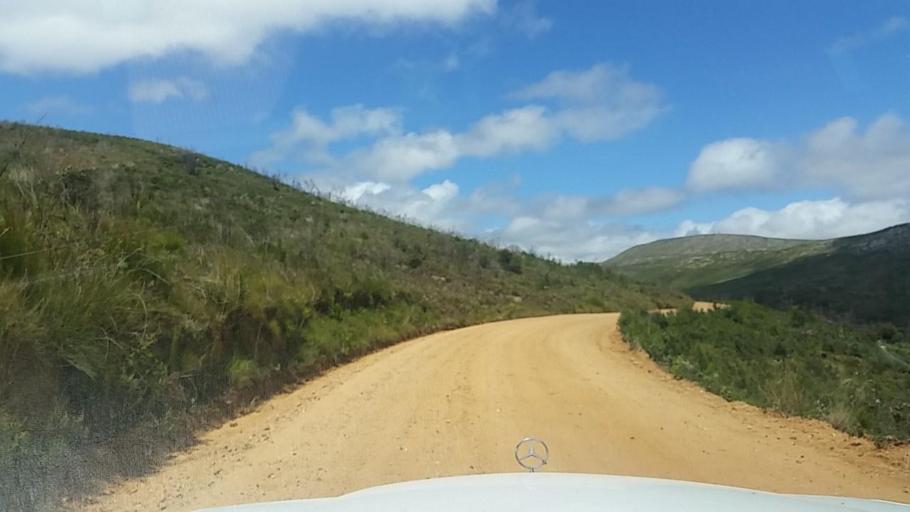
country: ZA
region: Western Cape
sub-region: Eden District Municipality
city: Knysna
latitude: -33.8758
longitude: 23.1497
